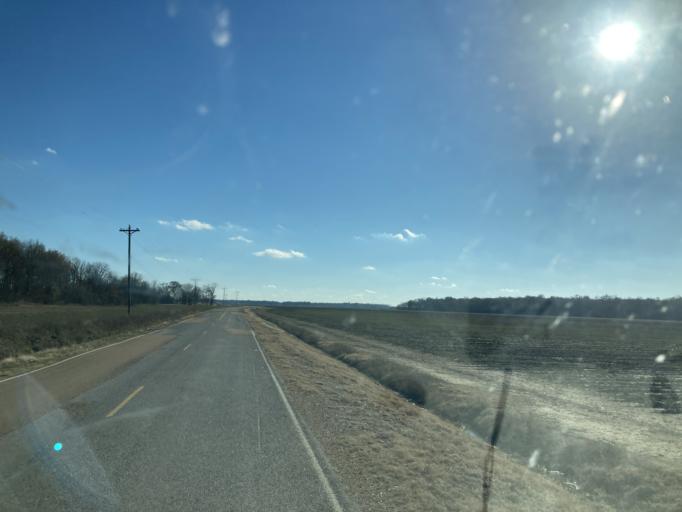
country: US
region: Mississippi
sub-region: Yazoo County
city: Yazoo City
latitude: 32.9476
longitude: -90.5081
